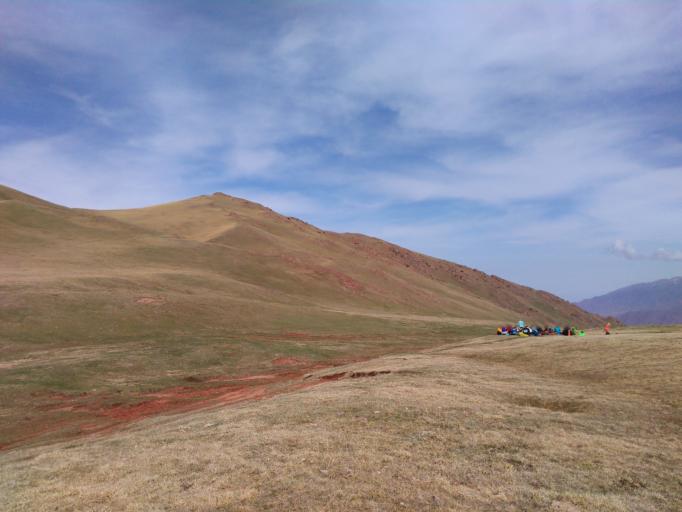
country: KG
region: Naryn
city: Kochkor
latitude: 42.4983
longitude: 75.7138
